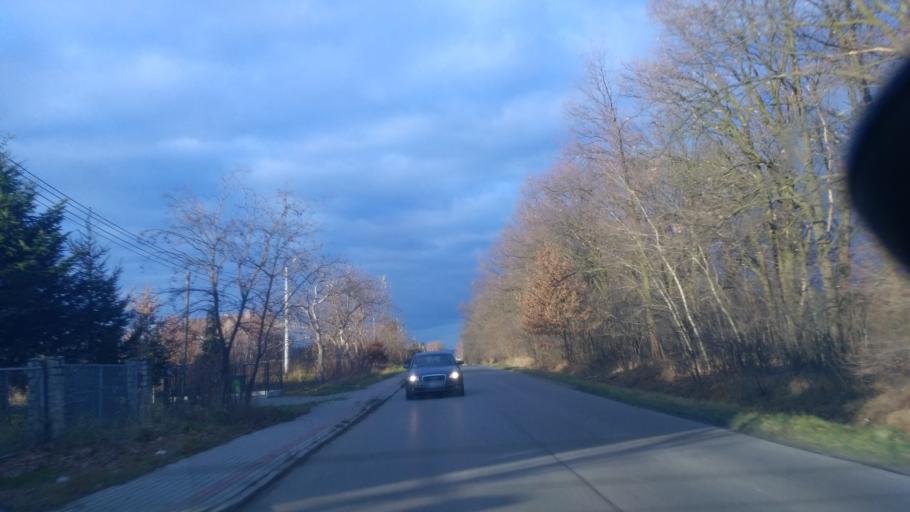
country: PL
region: Subcarpathian Voivodeship
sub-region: Powiat rzeszowski
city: Krasne
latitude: 50.0489
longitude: 22.1226
